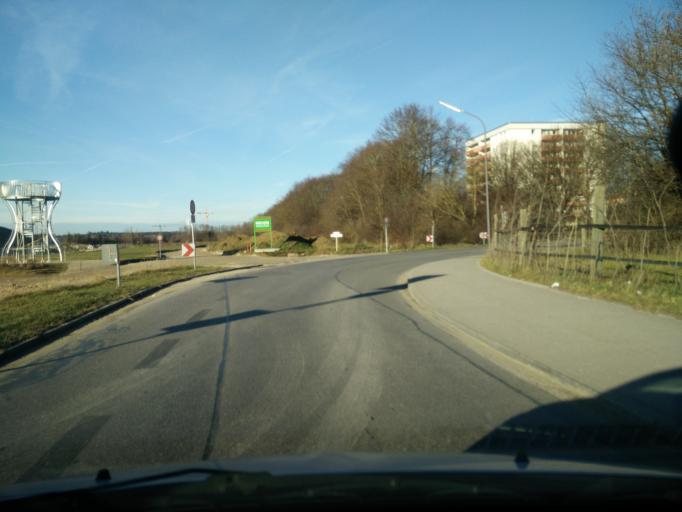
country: DE
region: Bavaria
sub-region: Upper Bavaria
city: Grafelfing
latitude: 48.1456
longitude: 11.4104
